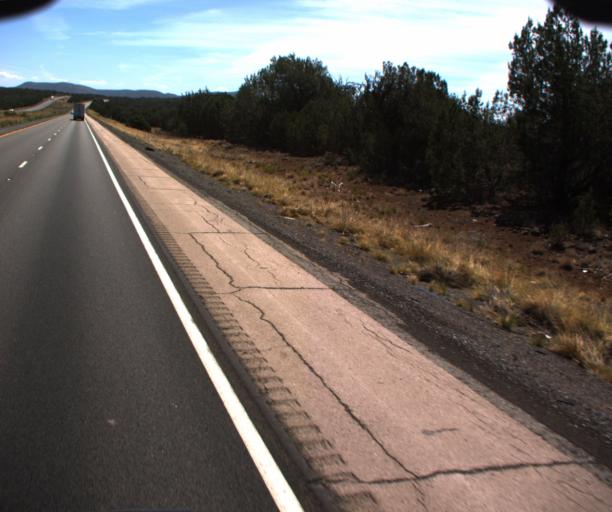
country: US
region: Arizona
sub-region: Mohave County
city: Peach Springs
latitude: 35.1909
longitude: -113.3441
